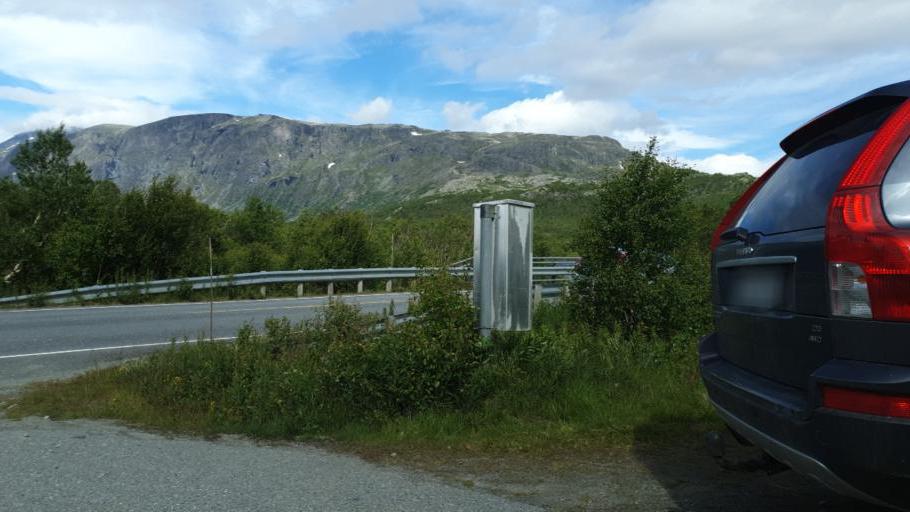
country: NO
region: Oppland
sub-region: Oystre Slidre
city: Heggenes
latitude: 61.4844
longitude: 8.8375
